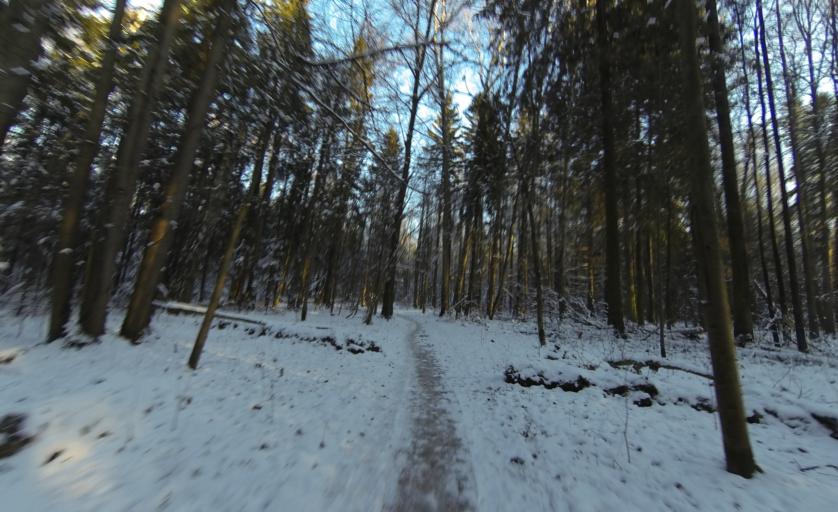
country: RU
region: Moscow
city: Metrogorodok
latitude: 55.8485
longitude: 37.7798
